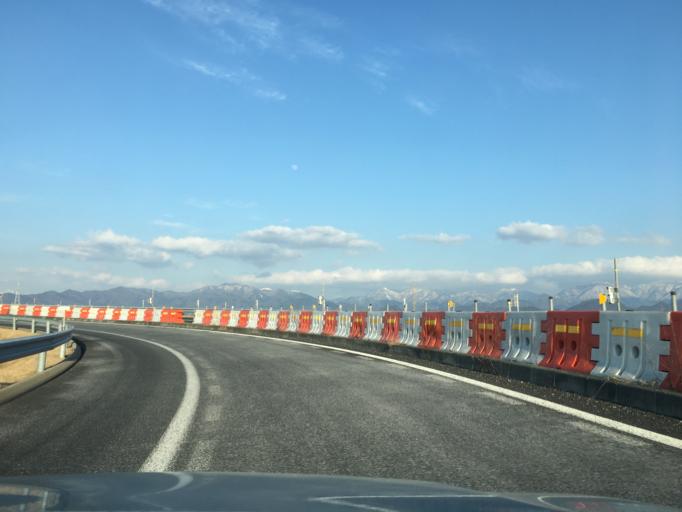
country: JP
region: Yamagata
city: Tendo
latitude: 38.3051
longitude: 140.3146
